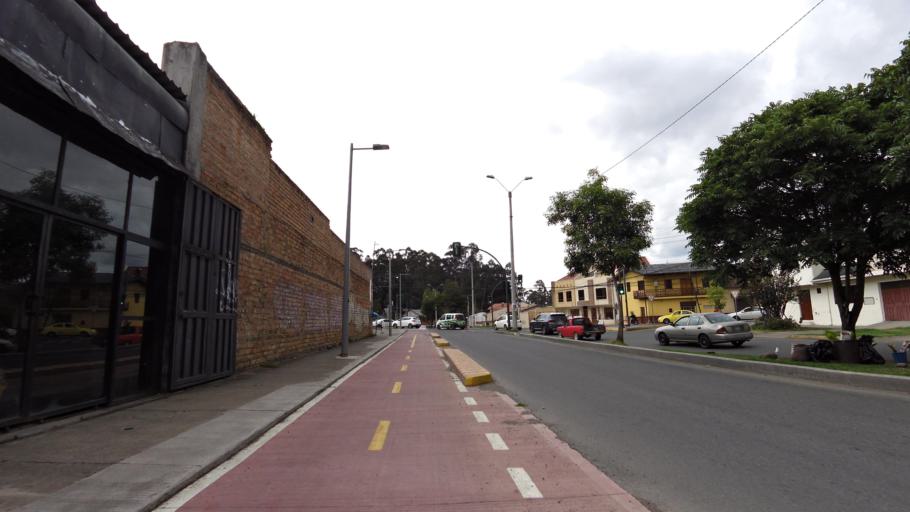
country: EC
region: Azuay
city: Cuenca
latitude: -2.9074
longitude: -79.0270
